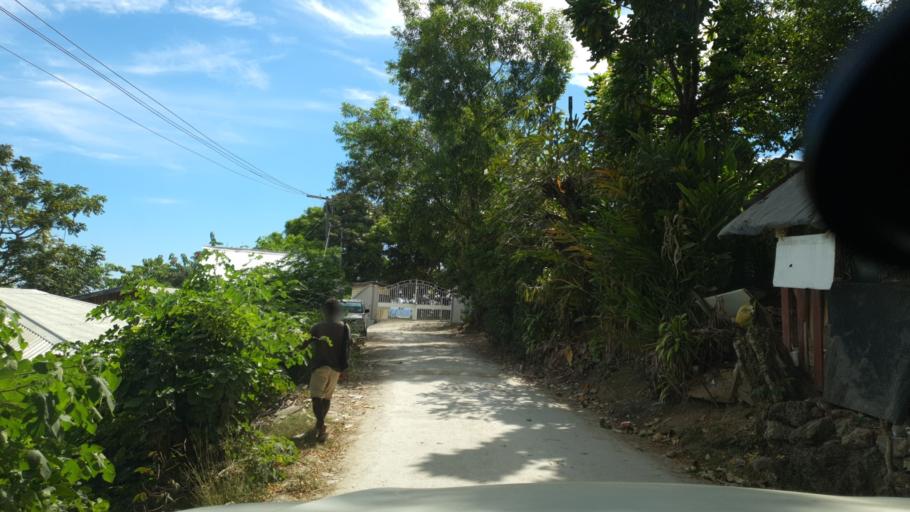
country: SB
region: Guadalcanal
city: Honiara
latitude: -9.4362
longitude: 159.9805
